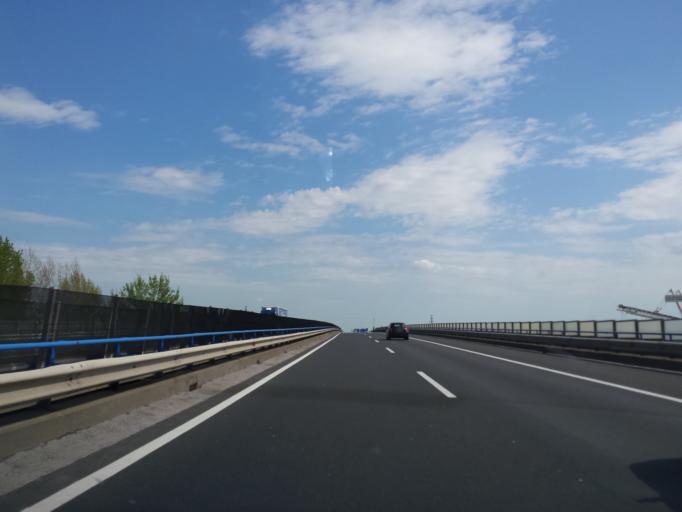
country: AT
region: Burgenland
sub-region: Politischer Bezirk Neusiedl am See
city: Nickelsdorf
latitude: 47.9040
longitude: 17.1529
